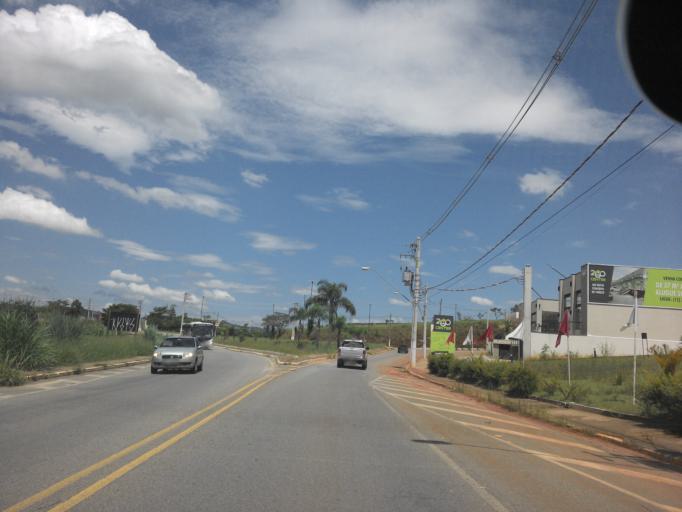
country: BR
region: Sao Paulo
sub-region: Taubate
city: Taubate
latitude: -23.0600
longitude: -45.5561
